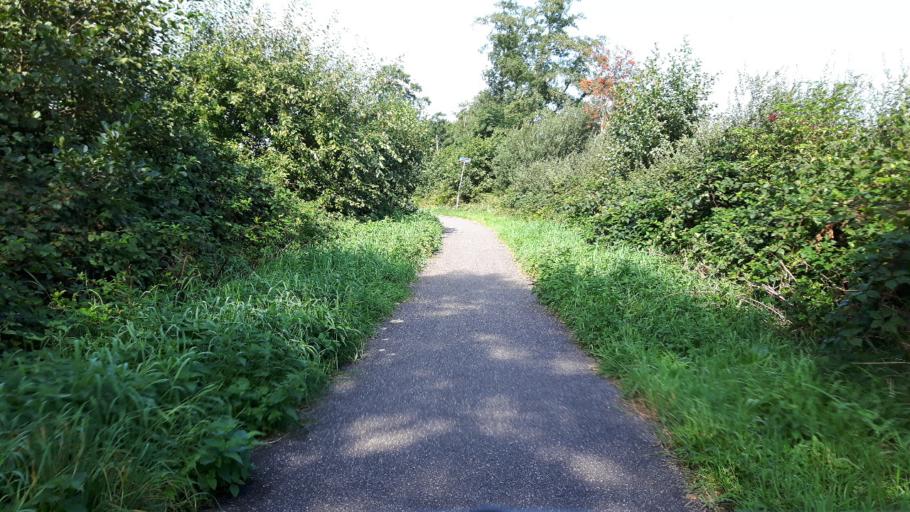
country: NL
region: Groningen
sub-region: Gemeente Leek
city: Leek
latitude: 53.1202
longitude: 6.4709
